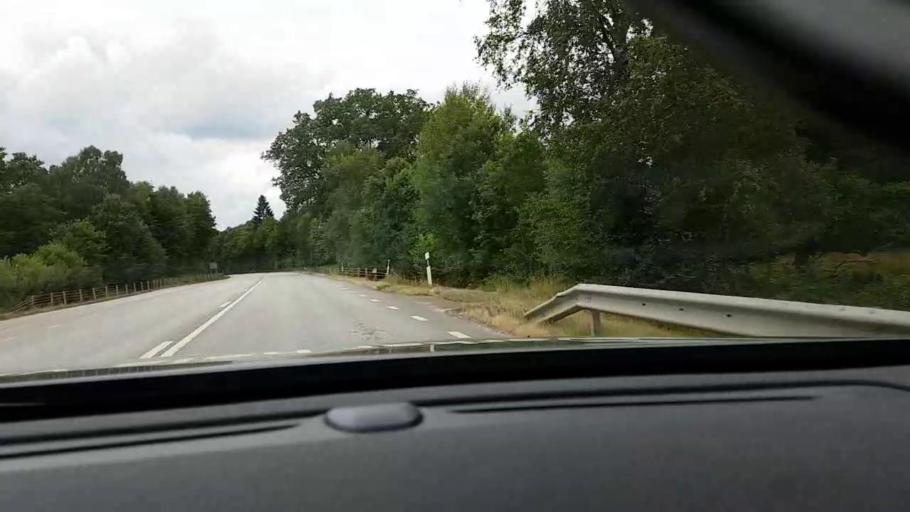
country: SE
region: Skane
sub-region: Horby Kommun
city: Hoerby
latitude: 55.8656
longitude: 13.6385
